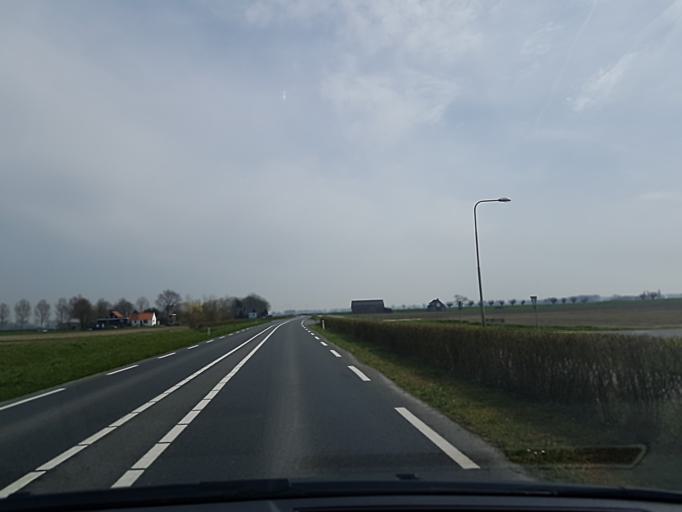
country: NL
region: Zeeland
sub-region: Gemeente Terneuzen
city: Zaamslag
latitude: 51.3117
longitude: 3.9488
